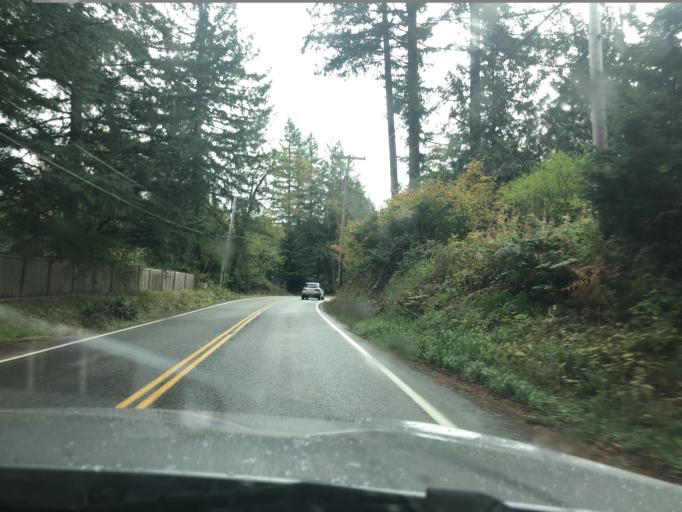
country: US
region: Washington
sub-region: King County
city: Riverbend
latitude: 47.4504
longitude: -121.7580
